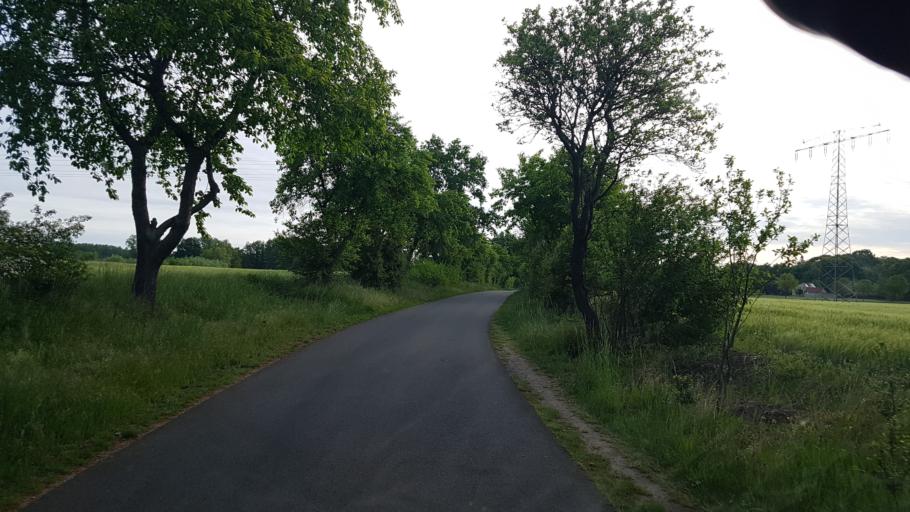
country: DE
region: Brandenburg
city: Luckau
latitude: 51.8161
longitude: 13.6426
